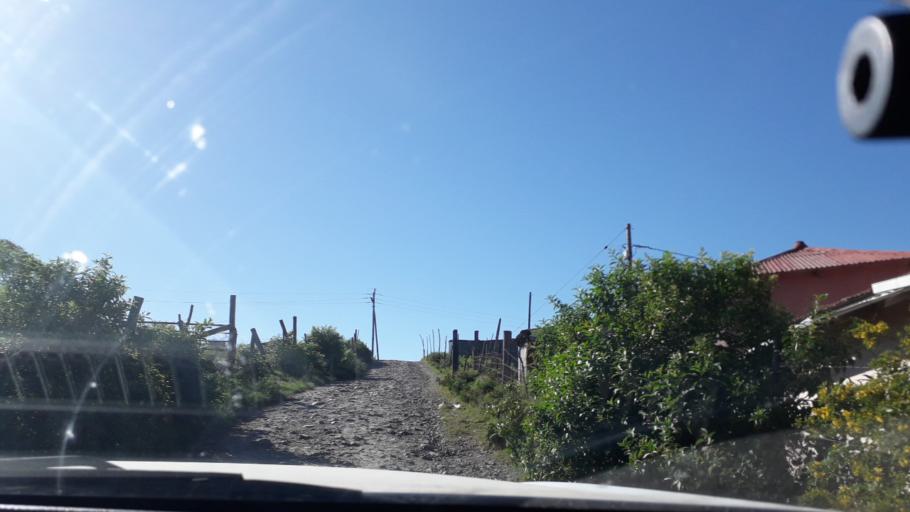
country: ZA
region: Eastern Cape
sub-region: Buffalo City Metropolitan Municipality
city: East London
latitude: -32.8453
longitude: 27.9862
